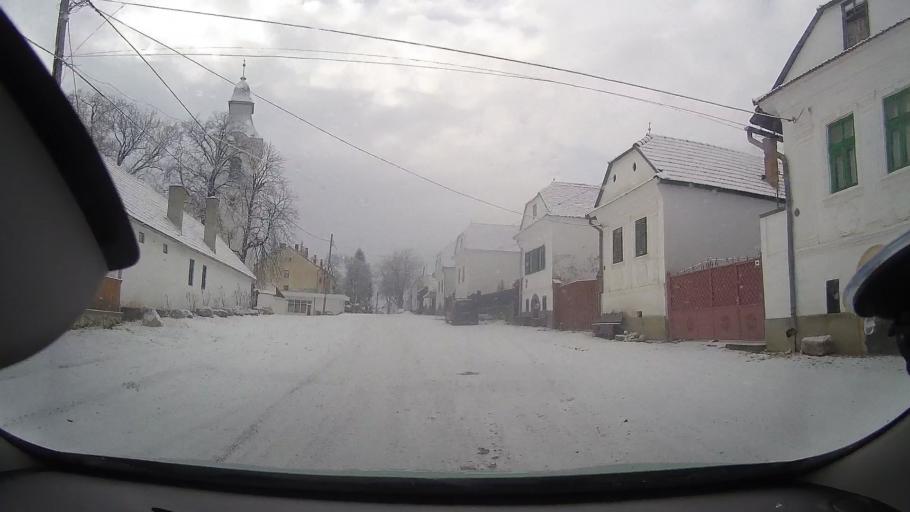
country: RO
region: Alba
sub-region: Comuna Rimetea
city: Rimetea
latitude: 46.4534
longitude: 23.5673
